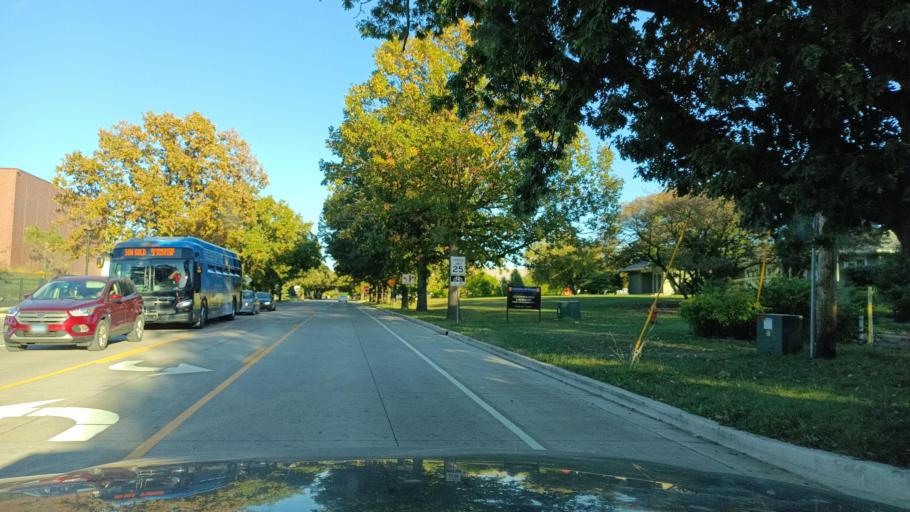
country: US
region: Illinois
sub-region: Champaign County
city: Champaign
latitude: 40.0944
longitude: -88.2433
